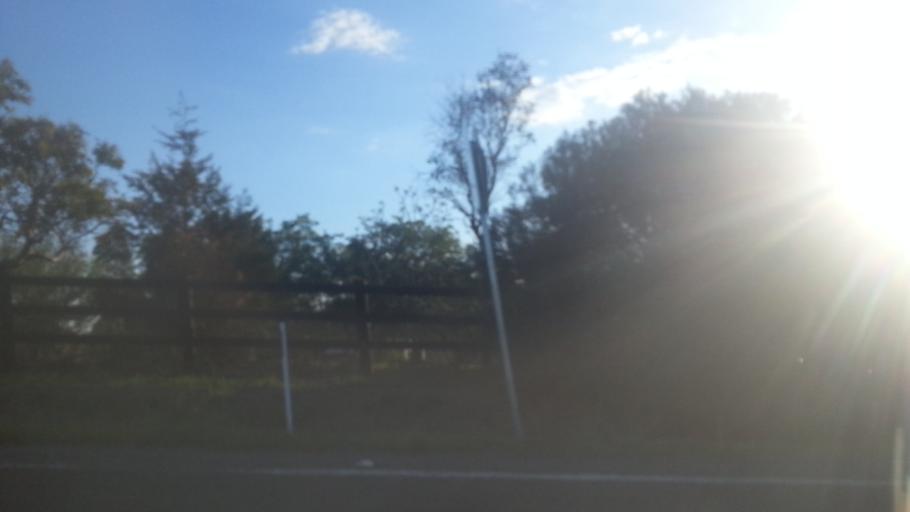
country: AU
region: New South Wales
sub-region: Wollondilly
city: Douglas Park
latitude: -34.1474
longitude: 150.7205
